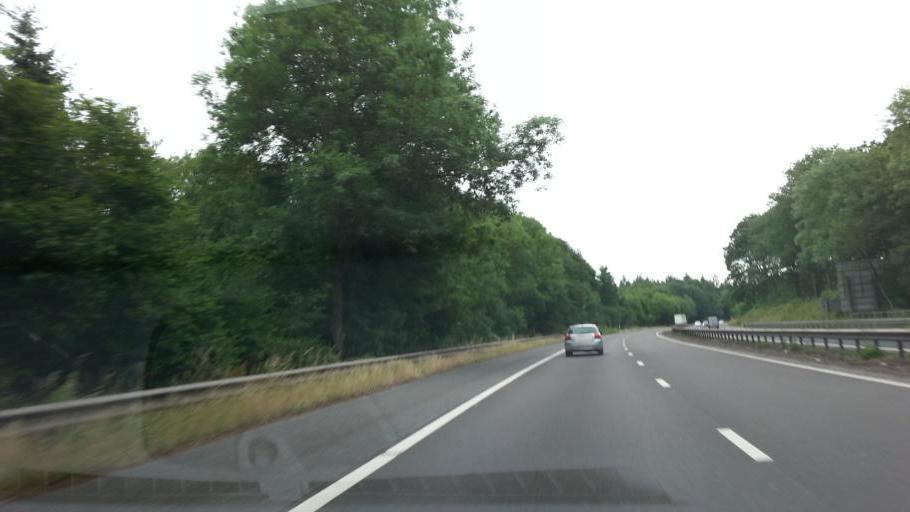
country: GB
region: England
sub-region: Herefordshire
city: Linton
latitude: 51.9386
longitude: -2.4771
